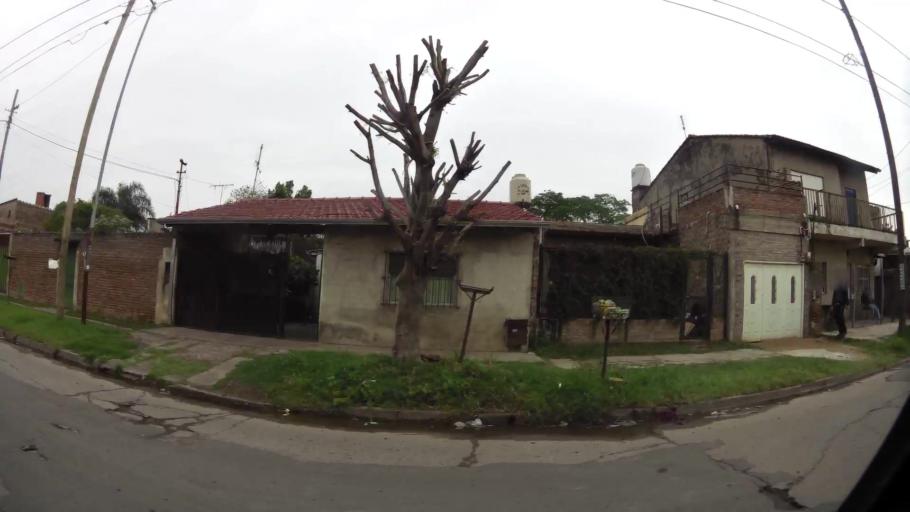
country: AR
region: Buenos Aires
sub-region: Partido de Lanus
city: Lanus
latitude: -34.7242
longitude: -58.3544
